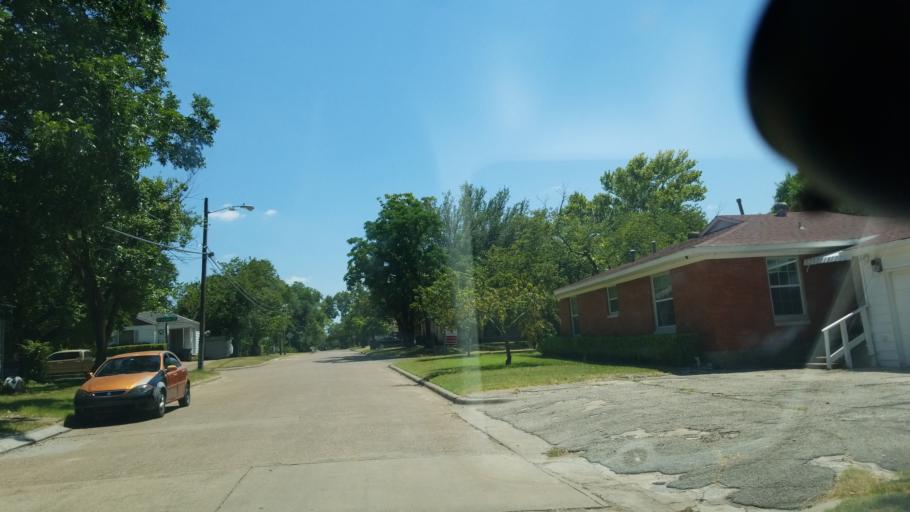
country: US
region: Texas
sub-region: Dallas County
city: Cockrell Hill
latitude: 32.7256
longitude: -96.8512
